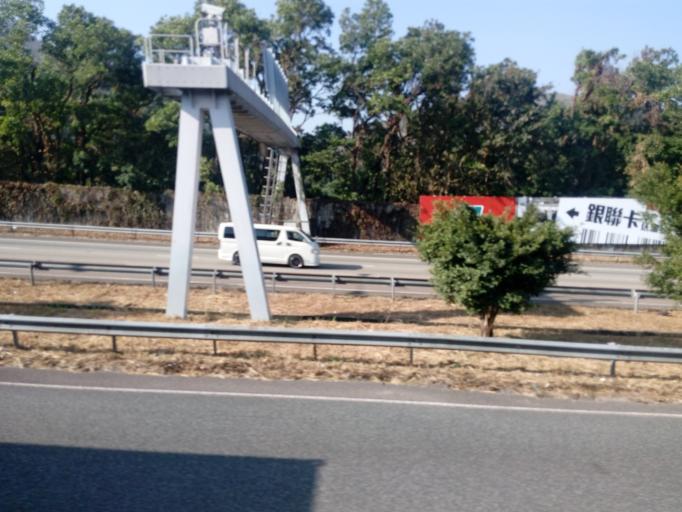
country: HK
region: Yuen Long
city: Yuen Long Kau Hui
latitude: 22.4318
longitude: 114.0630
